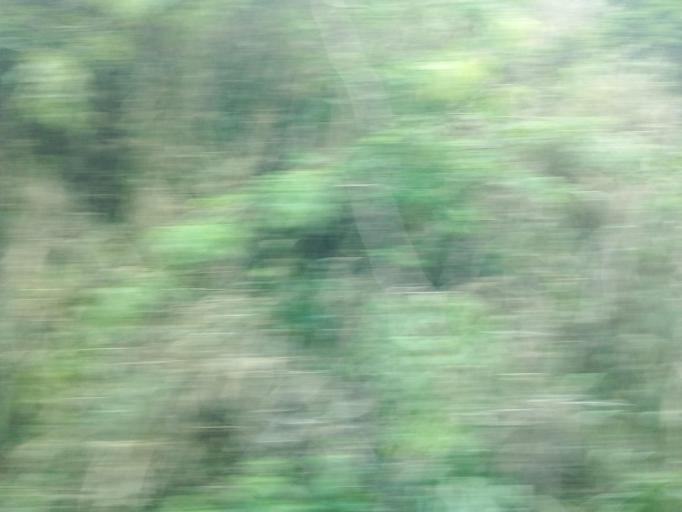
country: BR
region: Minas Gerais
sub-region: Timoteo
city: Timoteo
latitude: -19.5664
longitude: -42.7160
